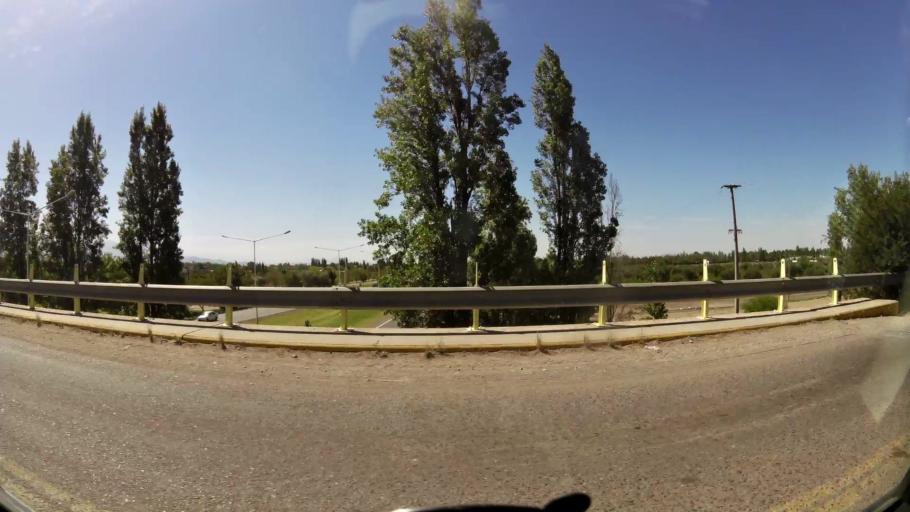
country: AR
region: Mendoza
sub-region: Departamento de Godoy Cruz
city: Godoy Cruz
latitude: -32.9846
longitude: -68.8493
